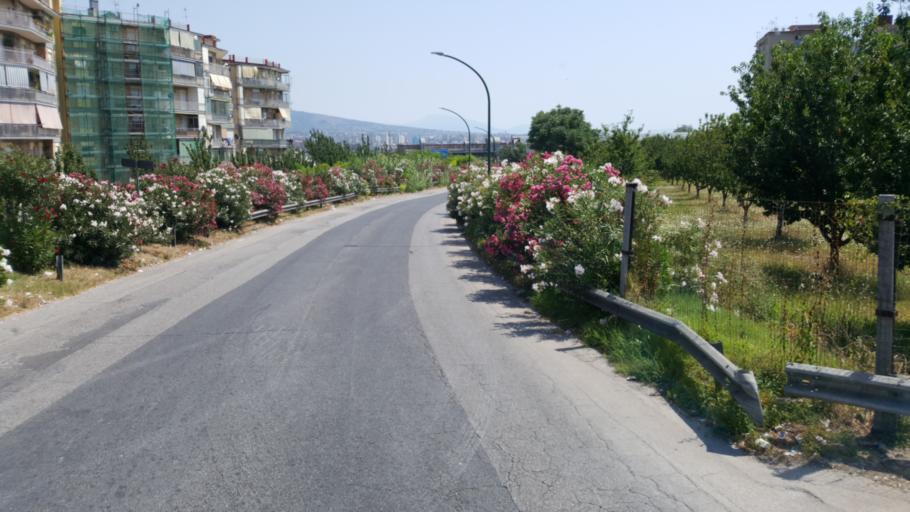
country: IT
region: Campania
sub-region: Provincia di Napoli
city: Arpino
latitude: 40.8834
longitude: 14.3165
